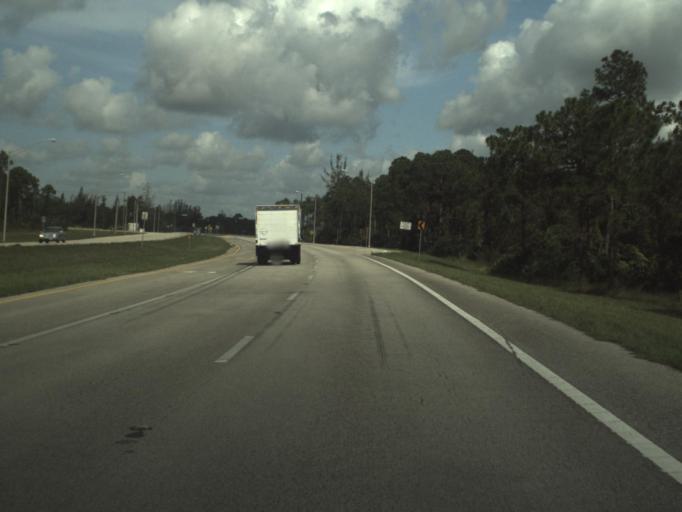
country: US
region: Florida
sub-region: Palm Beach County
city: Limestone Creek
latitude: 26.9019
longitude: -80.2875
